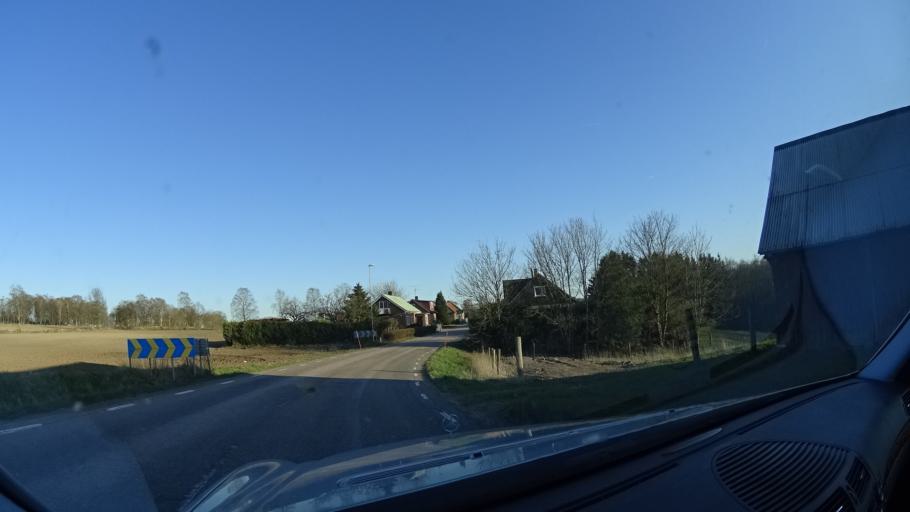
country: SE
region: Skane
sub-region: Bjuvs Kommun
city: Billesholm
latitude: 56.0535
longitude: 12.9979
